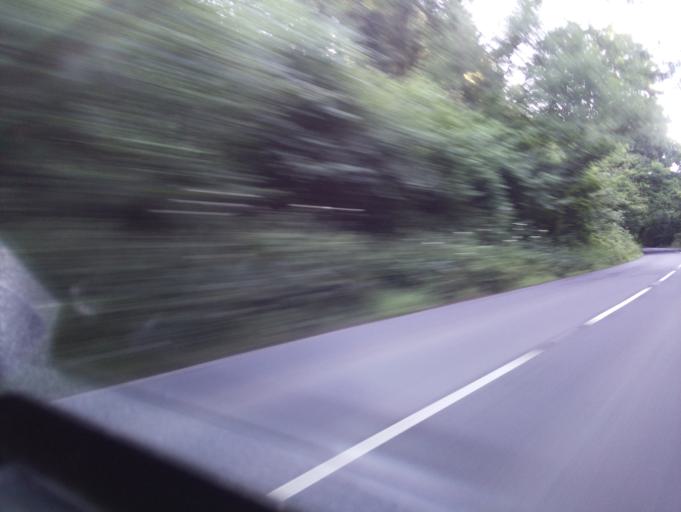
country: GB
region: Wales
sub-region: Monmouthshire
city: Monmouth
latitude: 51.7636
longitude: -2.6750
